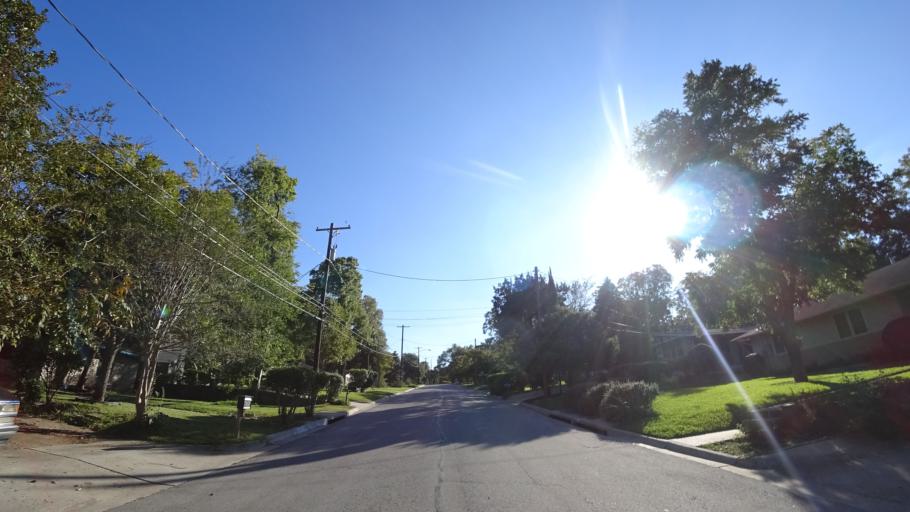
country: US
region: Texas
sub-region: Travis County
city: Austin
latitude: 30.2246
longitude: -97.7324
